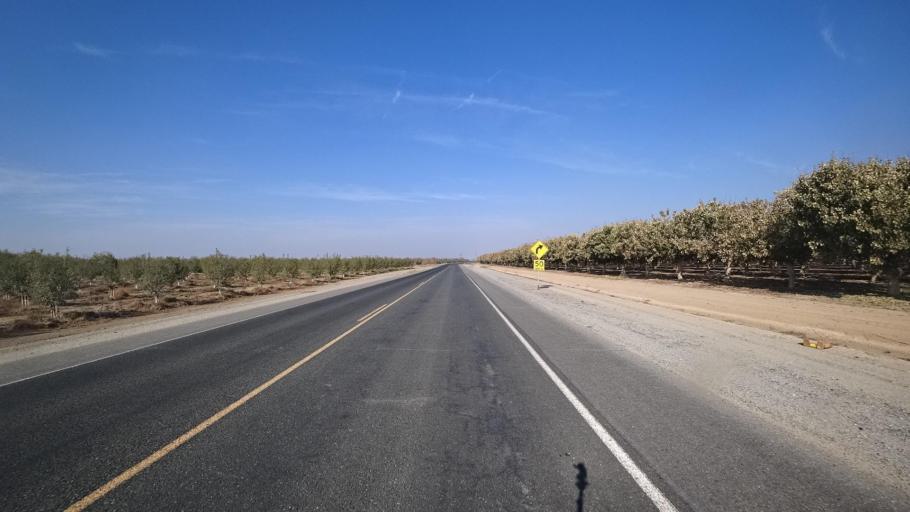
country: US
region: California
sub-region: Kern County
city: McFarland
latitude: 35.6560
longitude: -119.1957
